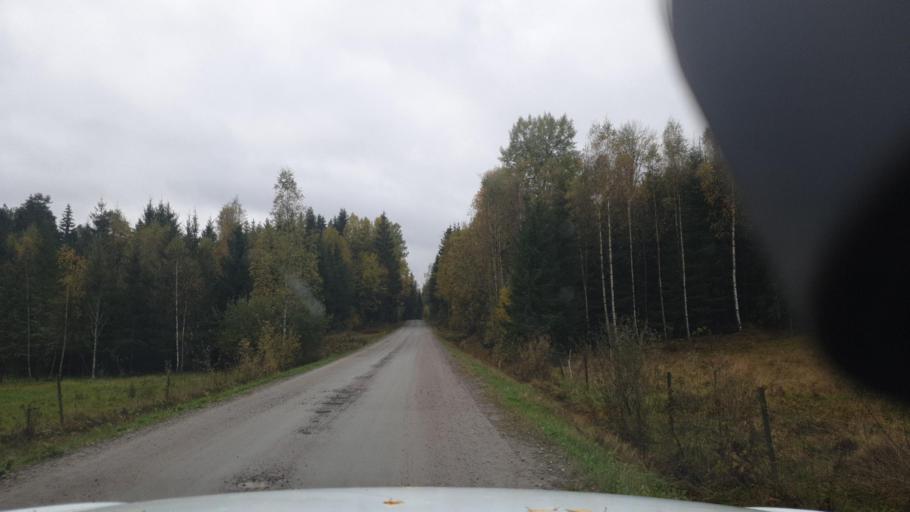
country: SE
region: Vaermland
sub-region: Karlstads Kommun
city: Edsvalla
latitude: 59.5021
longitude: 13.0308
